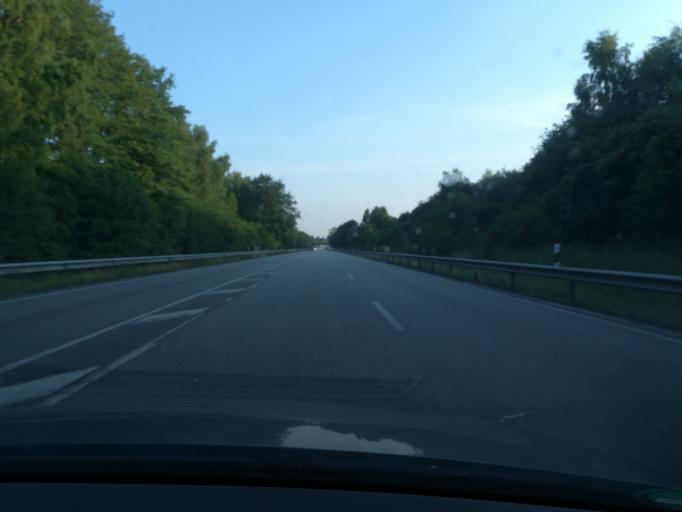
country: DE
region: Schleswig-Holstein
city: Grande
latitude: 53.5946
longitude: 10.3887
